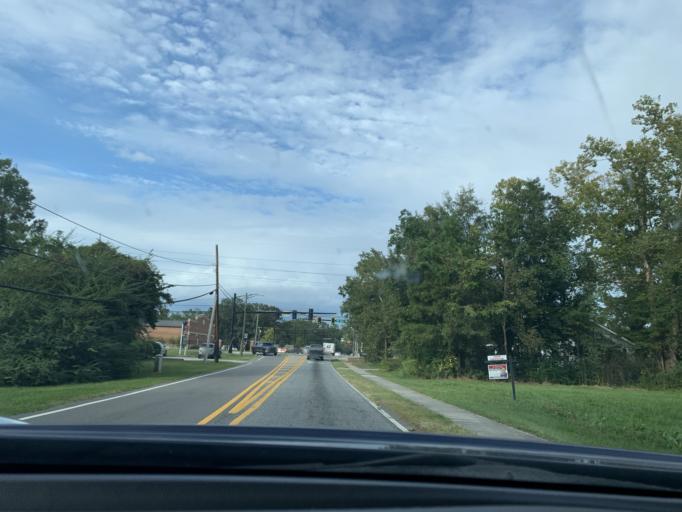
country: US
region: Georgia
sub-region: Chatham County
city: Pooler
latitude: 32.1143
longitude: -81.2494
